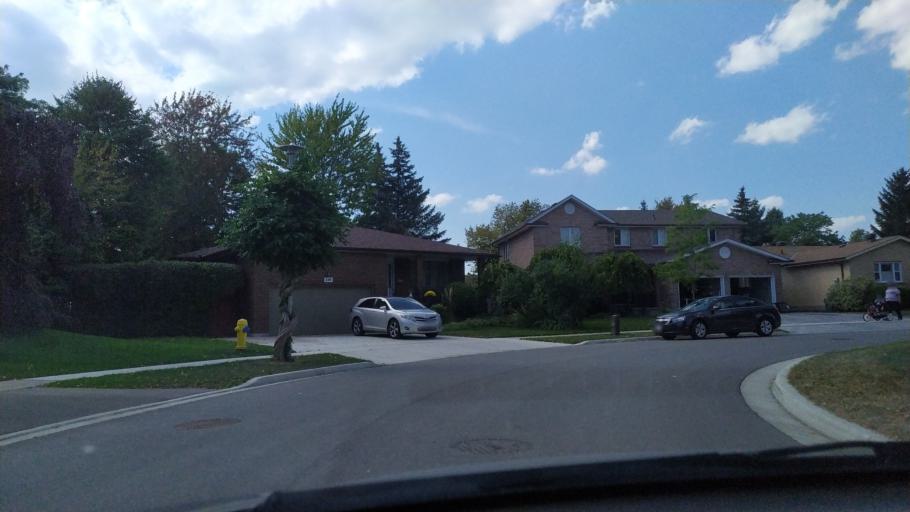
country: CA
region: Ontario
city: London
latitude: 42.9471
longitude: -81.2423
